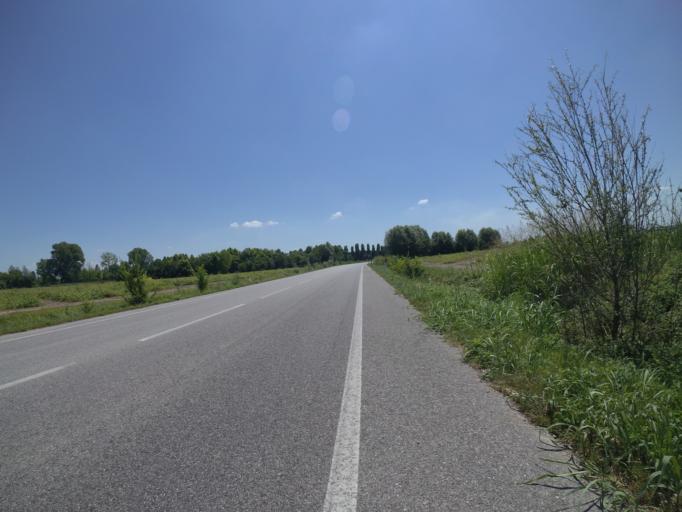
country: IT
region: Friuli Venezia Giulia
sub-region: Provincia di Udine
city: Varmo
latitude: 45.8847
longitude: 13.0101
